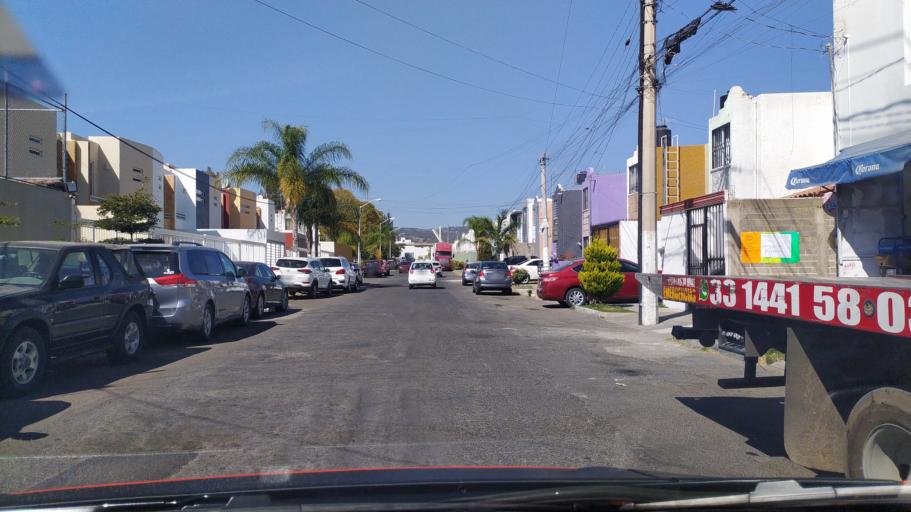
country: MX
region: Jalisco
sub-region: Tlajomulco de Zuniga
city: Palomar
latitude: 20.6288
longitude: -103.4626
